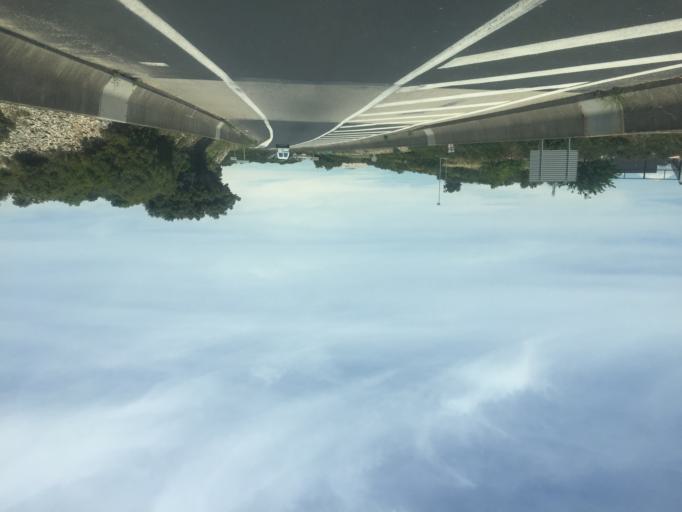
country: FR
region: Languedoc-Roussillon
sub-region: Departement du Gard
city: Les Angles
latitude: 43.9602
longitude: 4.7457
